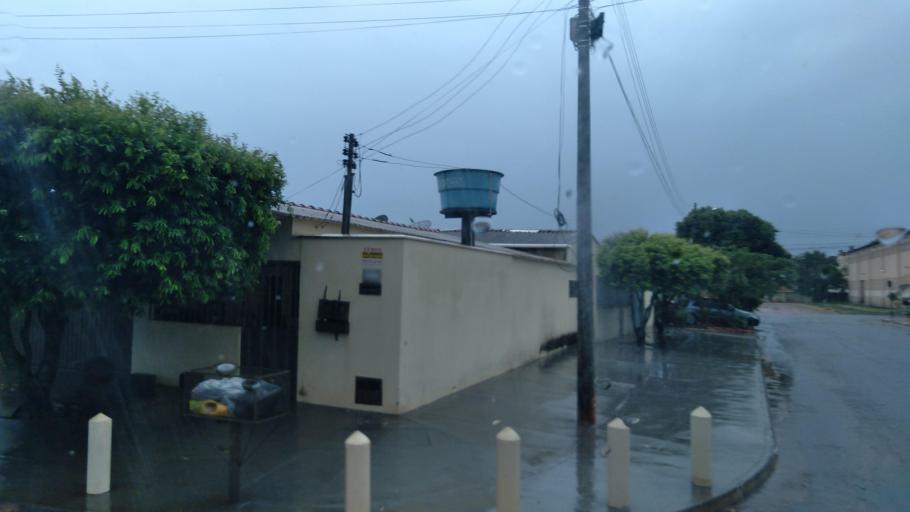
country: BR
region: Goias
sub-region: Mineiros
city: Mineiros
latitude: -17.5403
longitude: -52.5446
